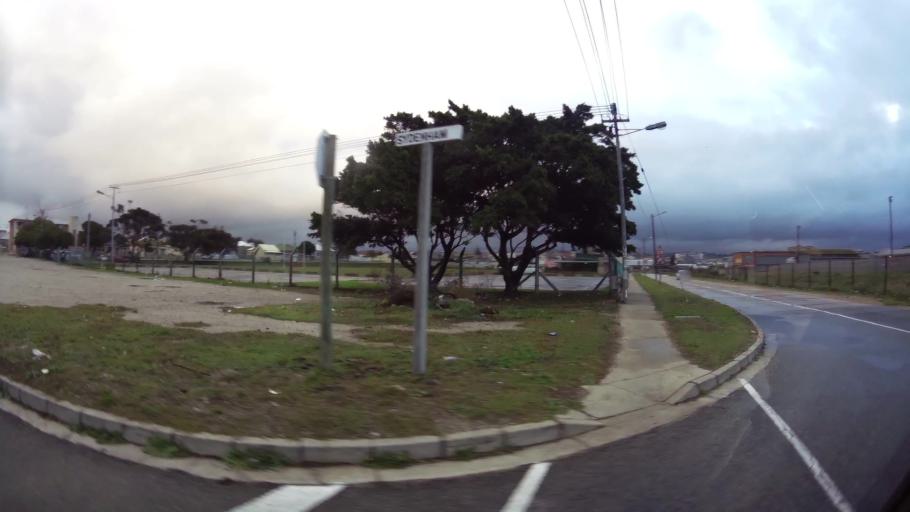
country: ZA
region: Eastern Cape
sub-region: Nelson Mandela Bay Metropolitan Municipality
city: Port Elizabeth
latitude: -33.9273
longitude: 25.5969
